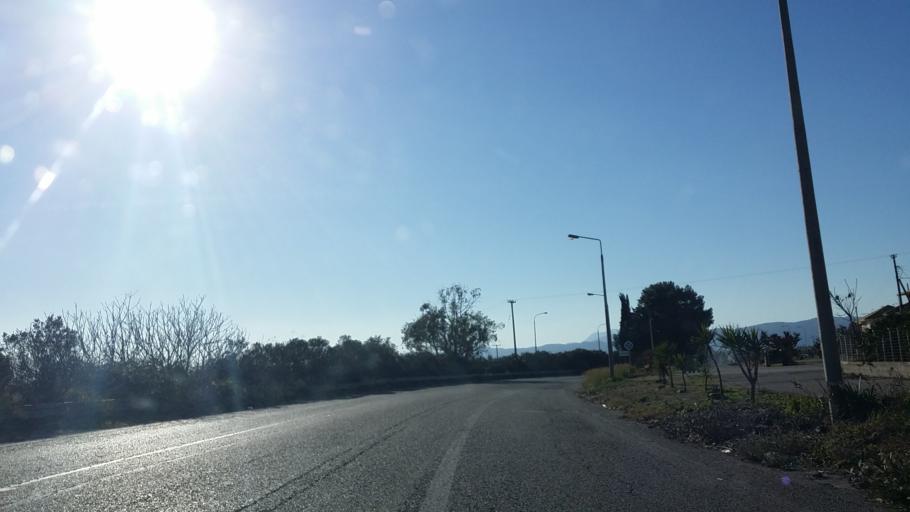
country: GR
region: West Greece
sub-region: Nomos Aitolias kai Akarnanias
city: Neapolis
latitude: 38.6678
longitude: 21.3215
